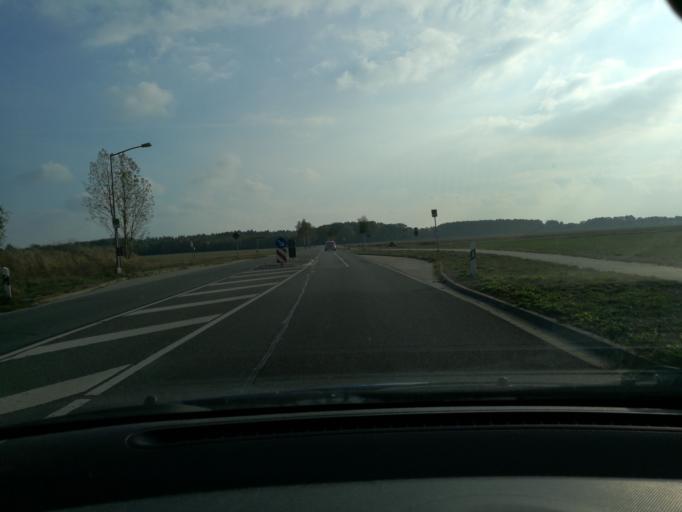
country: DE
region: Lower Saxony
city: Kusten
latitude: 53.0056
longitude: 11.1051
